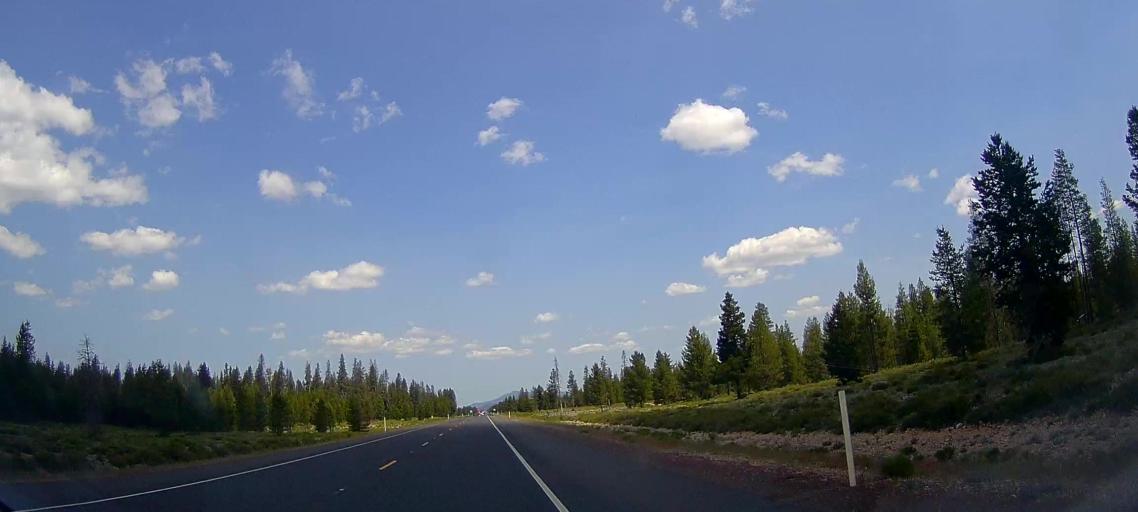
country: US
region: Oregon
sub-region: Deschutes County
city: La Pine
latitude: 43.0891
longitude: -121.8218
